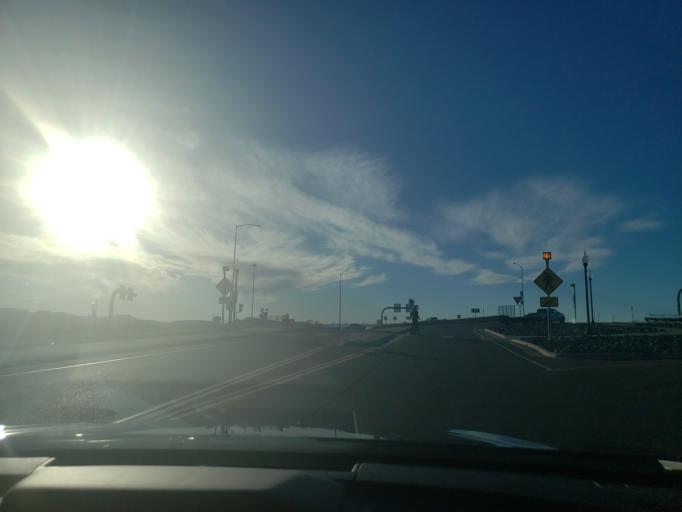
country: US
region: Colorado
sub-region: Mesa County
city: Fruita
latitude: 39.1542
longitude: -108.7369
